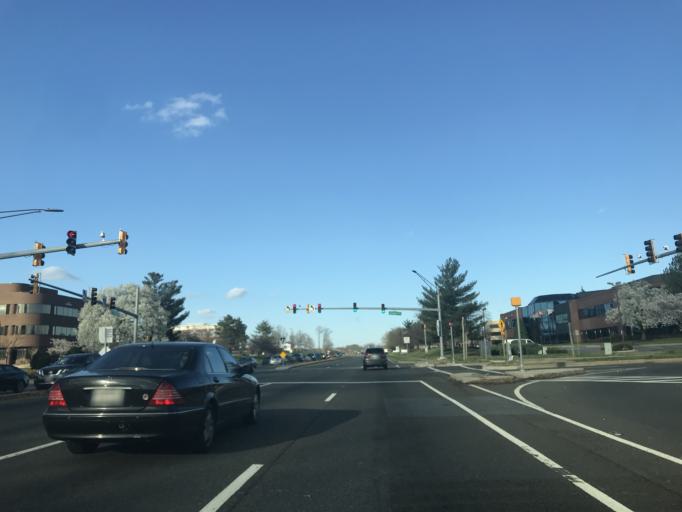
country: US
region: Maryland
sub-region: Prince George's County
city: Springdale
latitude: 38.9521
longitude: -76.8349
